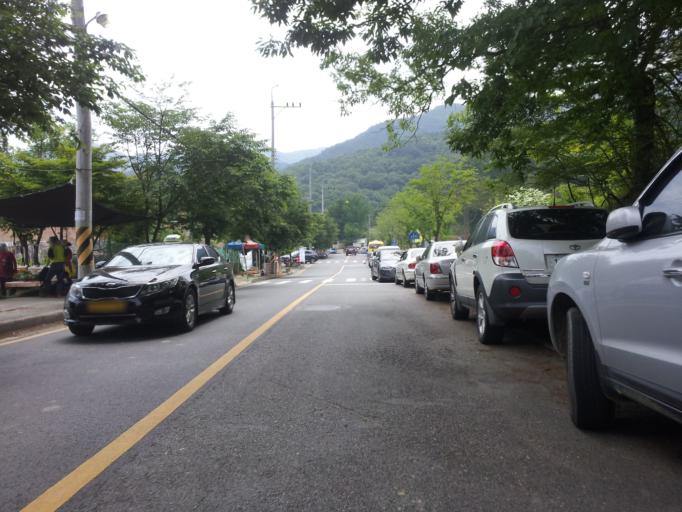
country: KR
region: Daejeon
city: Daejeon
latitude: 36.3305
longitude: 127.4821
